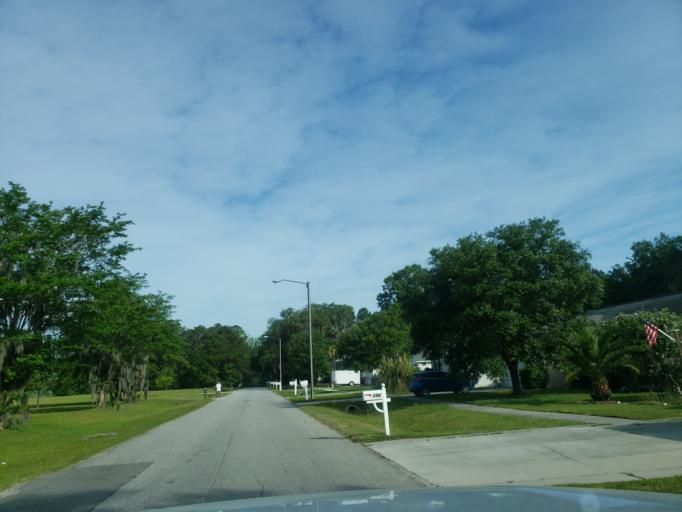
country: US
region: Georgia
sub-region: Chatham County
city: Georgetown
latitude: 32.0053
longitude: -81.2299
